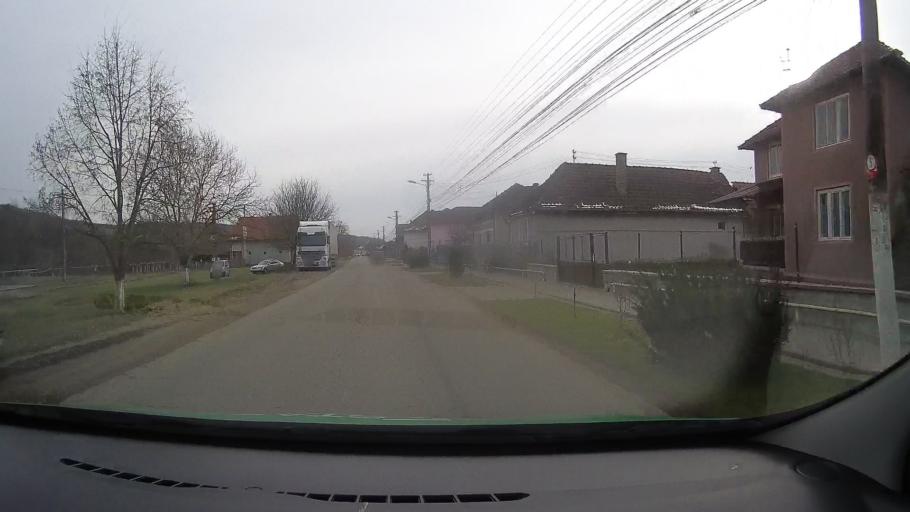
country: RO
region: Hunedoara
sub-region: Comuna Geoagiu
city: Geoagiu
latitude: 45.9328
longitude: 23.1941
